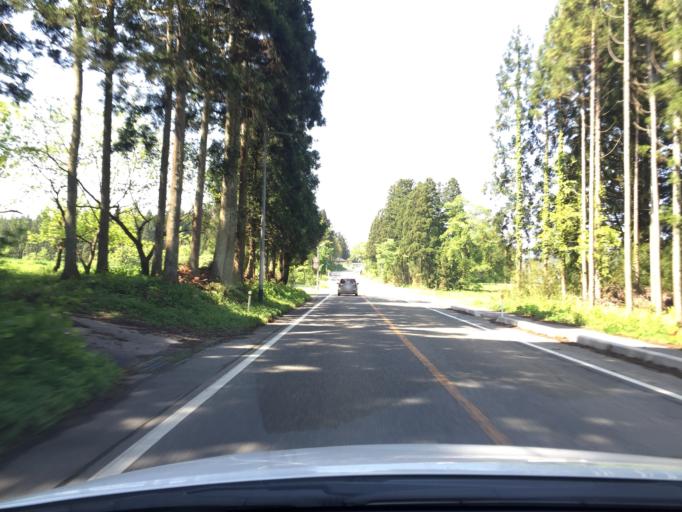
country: JP
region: Niigata
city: Muramatsu
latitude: 37.6680
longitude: 139.1432
